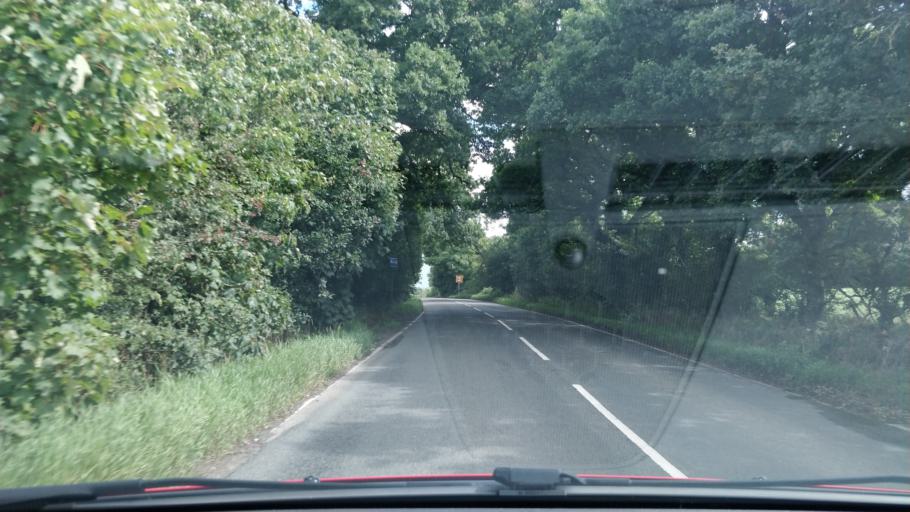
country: GB
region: Wales
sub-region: County of Flintshire
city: Hope
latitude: 53.1123
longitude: -3.0231
